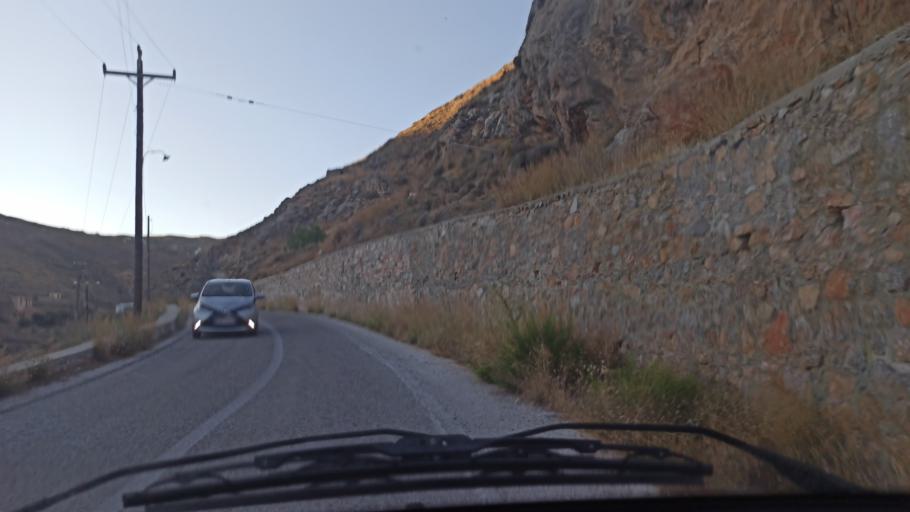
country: GR
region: South Aegean
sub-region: Nomos Kykladon
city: Ano Syros
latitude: 37.4554
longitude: 24.9332
